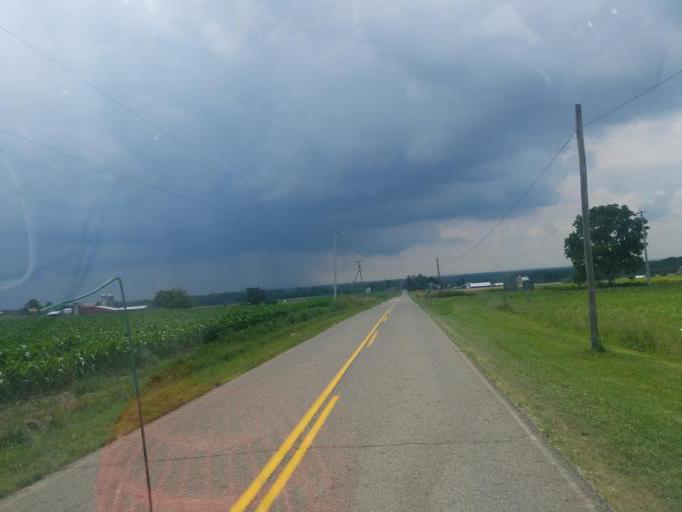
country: US
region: Ohio
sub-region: Mahoning County
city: Sebring
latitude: 40.9741
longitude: -80.9312
